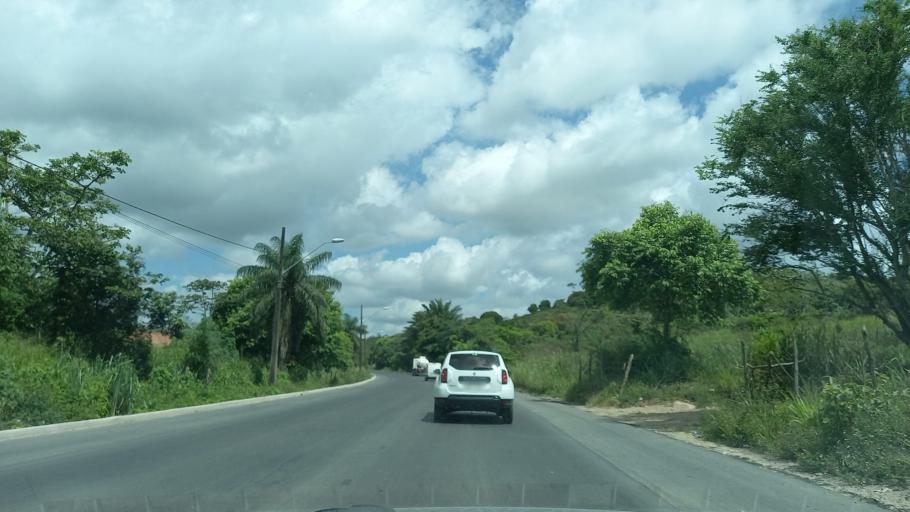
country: BR
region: Pernambuco
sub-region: Jaboatao Dos Guararapes
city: Jaboatao
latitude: -8.1460
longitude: -34.9999
